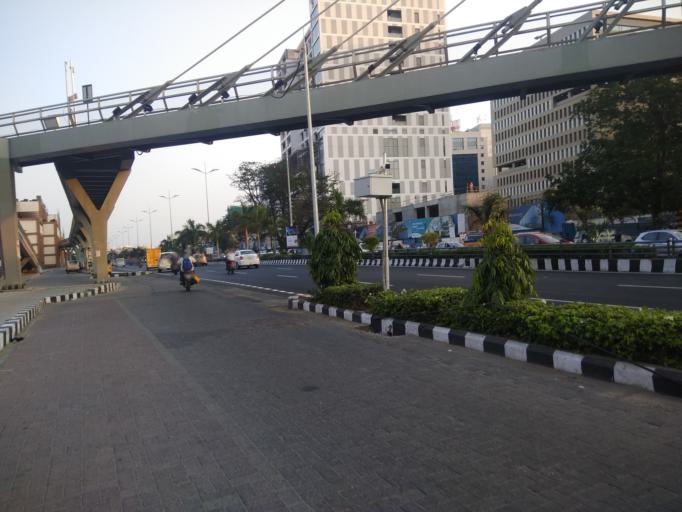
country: IN
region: Tamil Nadu
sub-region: Chennai
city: Gandhi Nagar
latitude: 12.9922
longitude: 80.2504
